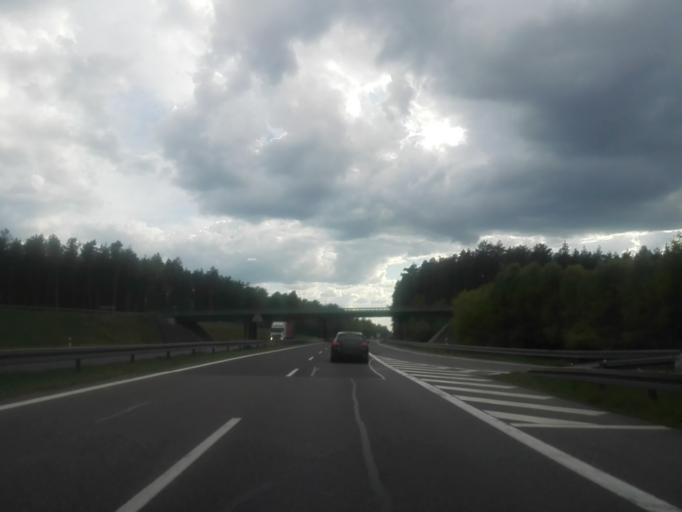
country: PL
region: Masovian Voivodeship
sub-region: Powiat ostrowski
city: Ostrow Mazowiecka
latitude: 52.7854
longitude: 21.8606
